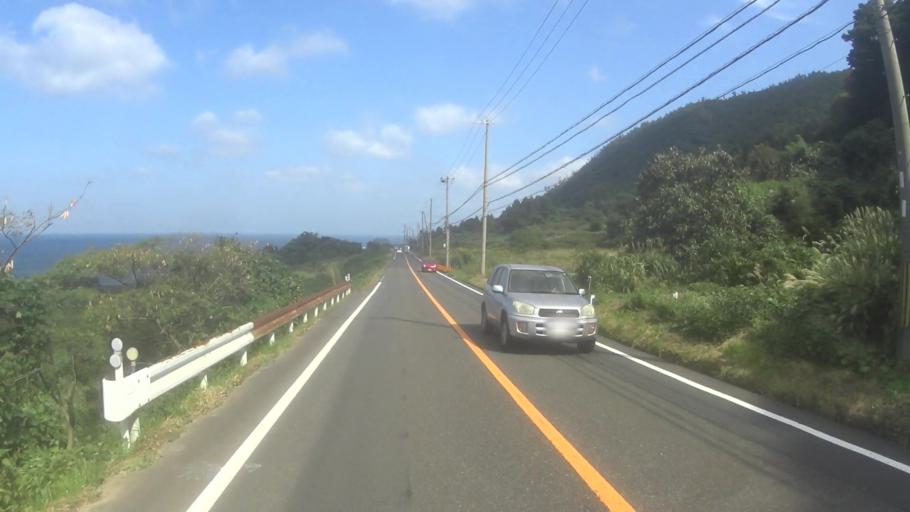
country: JP
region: Kyoto
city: Miyazu
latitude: 35.7489
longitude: 135.1478
